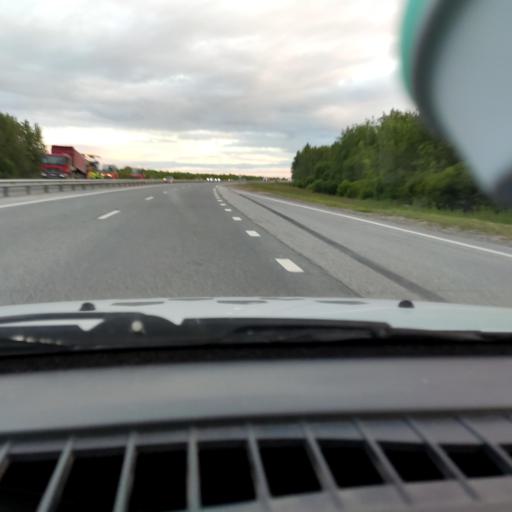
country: RU
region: Perm
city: Polazna
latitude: 58.2282
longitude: 56.4246
